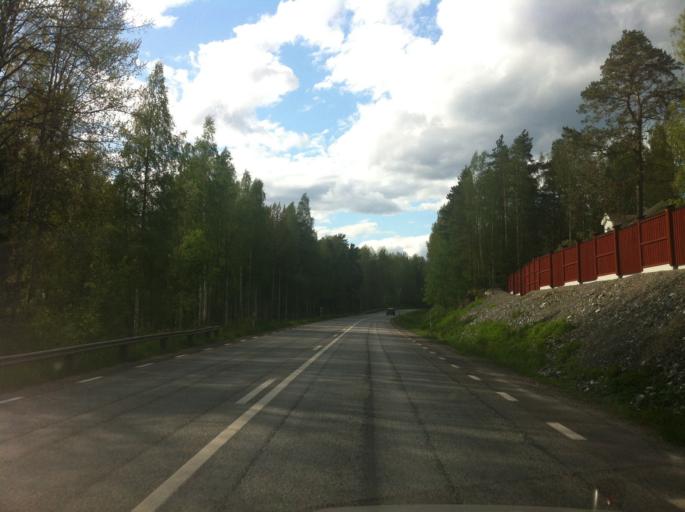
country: SE
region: Vaermland
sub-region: Filipstads Kommun
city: Filipstad
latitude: 59.6908
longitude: 14.1944
